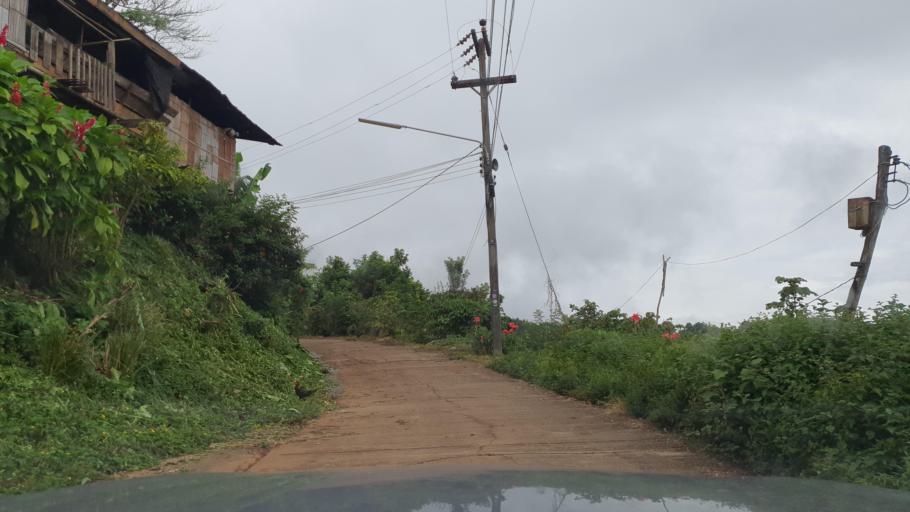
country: TH
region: Chiang Mai
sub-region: Amphoe Chiang Dao
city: Chiang Dao
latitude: 19.2605
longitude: 98.9218
